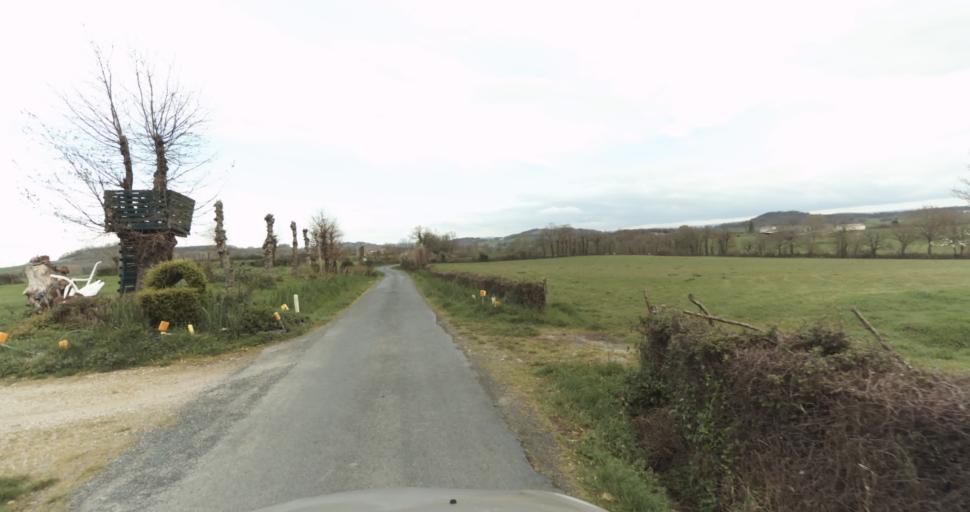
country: FR
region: Midi-Pyrenees
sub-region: Departement du Tarn
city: Frejairolles
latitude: 43.8732
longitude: 2.2048
